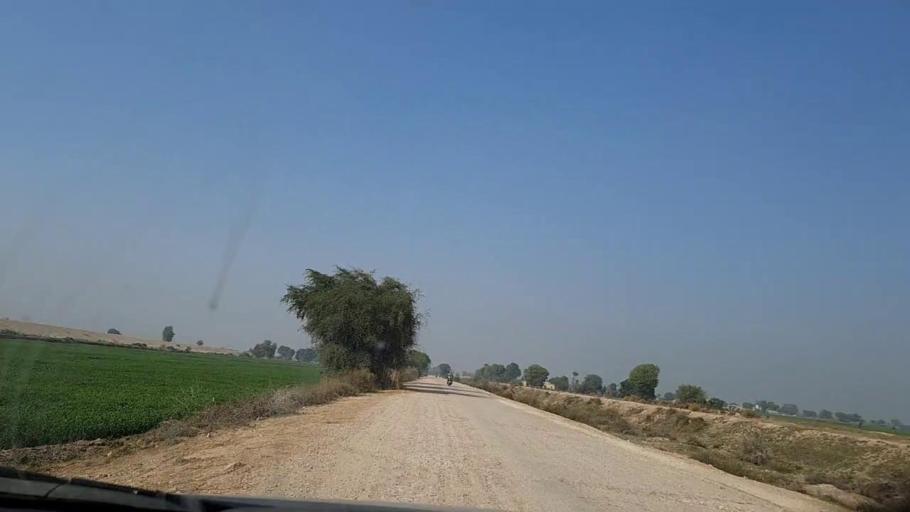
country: PK
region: Sindh
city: Moro
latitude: 26.7318
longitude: 67.9205
